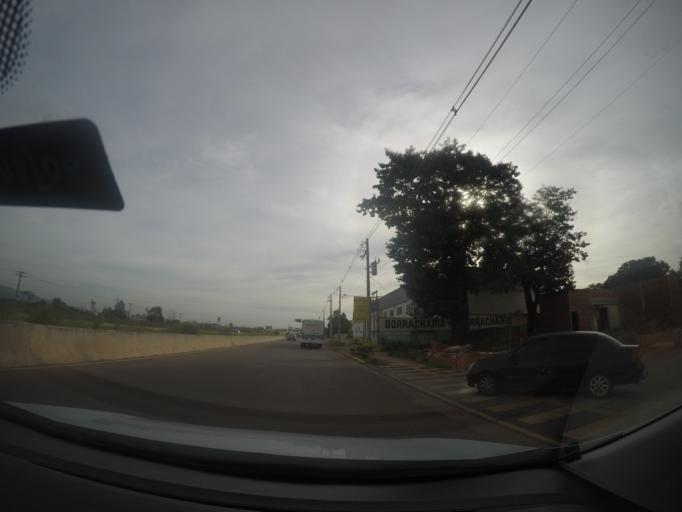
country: BR
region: Goias
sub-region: Goiania
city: Goiania
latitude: -16.7059
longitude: -49.3453
